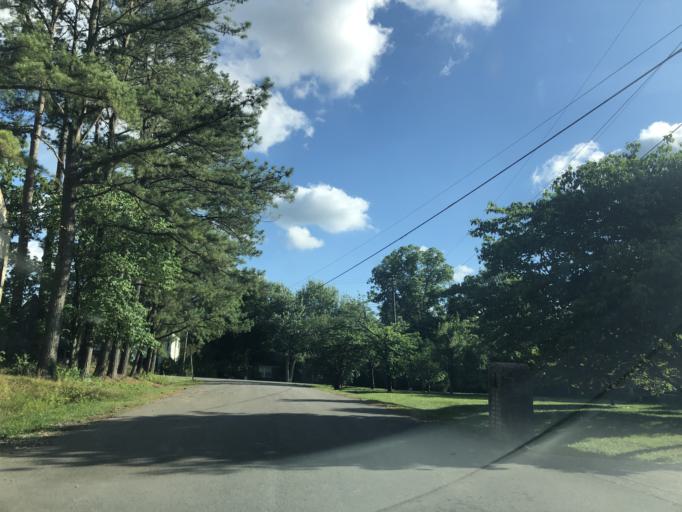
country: US
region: Tennessee
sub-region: Davidson County
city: Oak Hill
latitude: 36.0977
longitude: -86.8082
